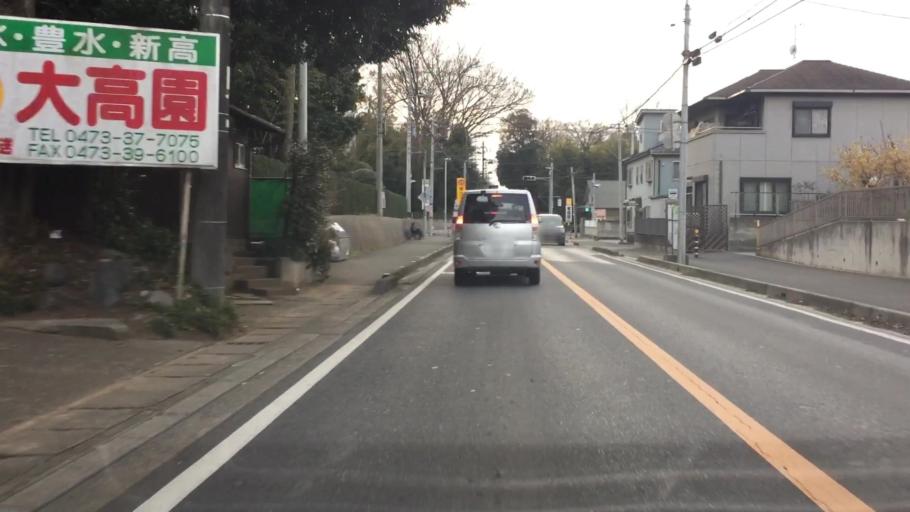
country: JP
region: Chiba
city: Matsudo
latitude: 35.7681
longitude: 139.9599
